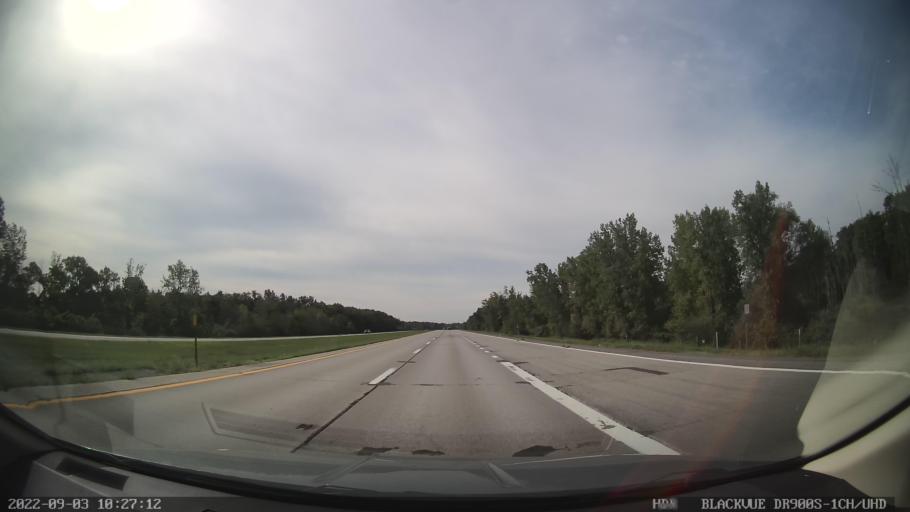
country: US
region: New York
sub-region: Livingston County
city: Livonia
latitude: 42.8209
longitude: -77.7374
